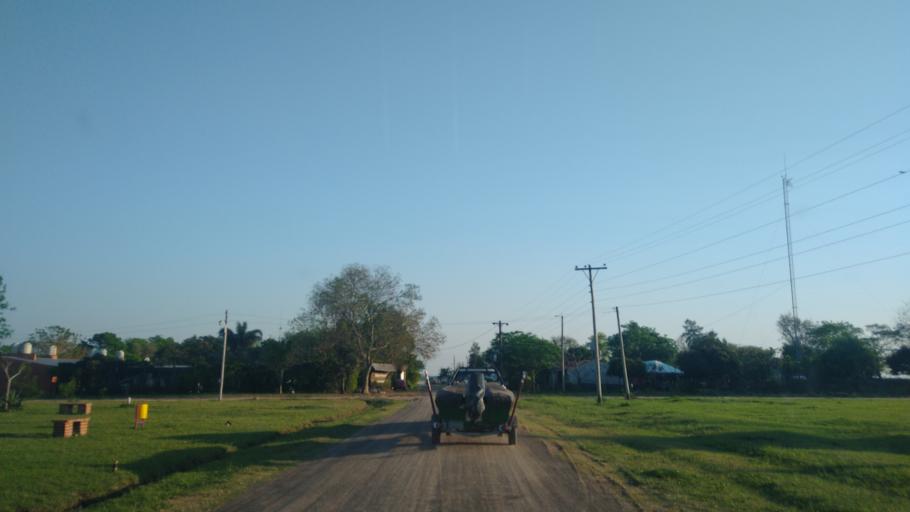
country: PY
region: Neembucu
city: Cerrito
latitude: -27.3720
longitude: -57.6552
